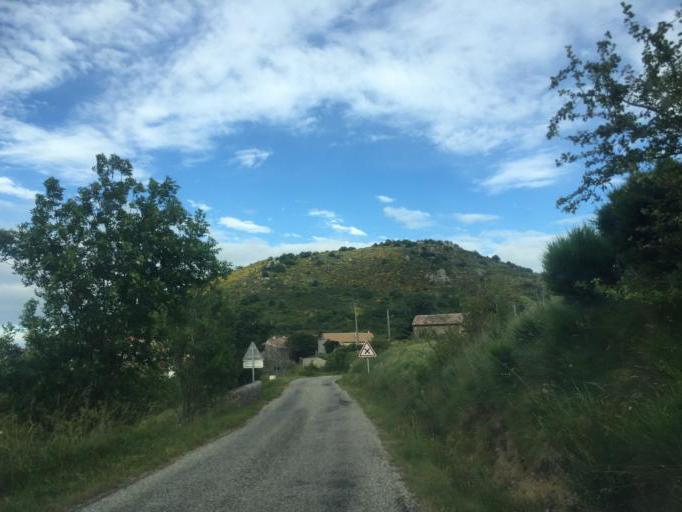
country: FR
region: Rhone-Alpes
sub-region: Departement de l'Ardeche
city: Saint-Julien-en-Saint-Alban
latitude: 44.7937
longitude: 4.6837
